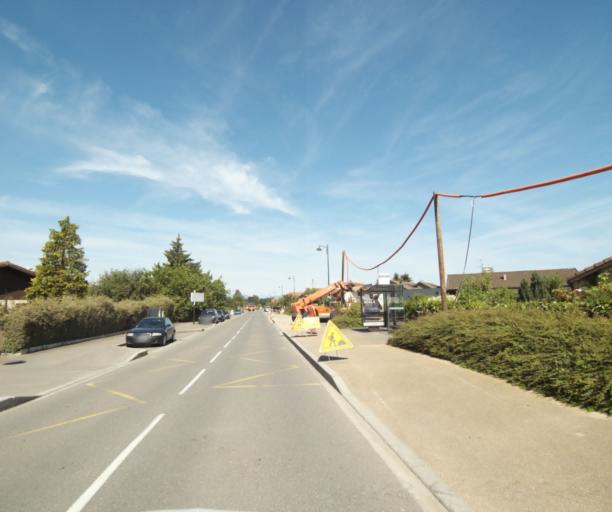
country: FR
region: Rhone-Alpes
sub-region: Departement de la Haute-Savoie
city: Thonon-les-Bains
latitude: 46.3853
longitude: 6.4974
